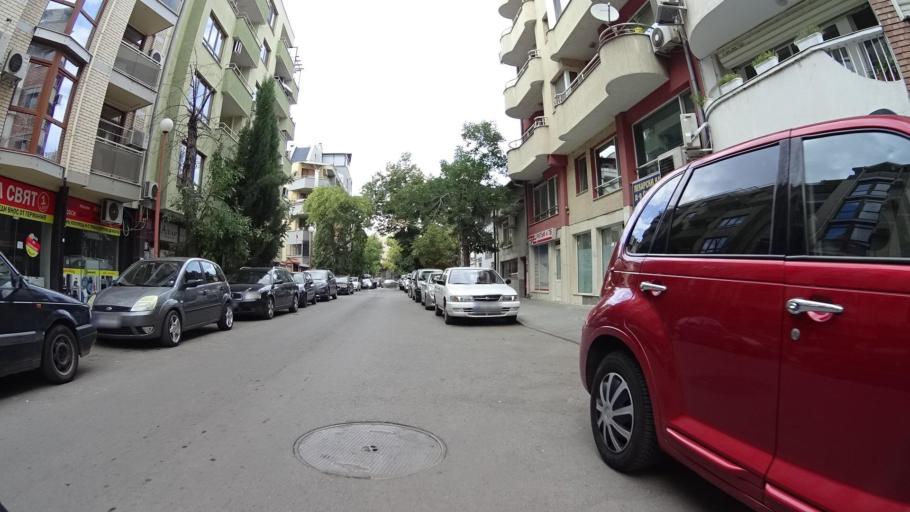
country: BG
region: Plovdiv
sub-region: Obshtina Plovdiv
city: Plovdiv
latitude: 42.1558
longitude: 24.7404
